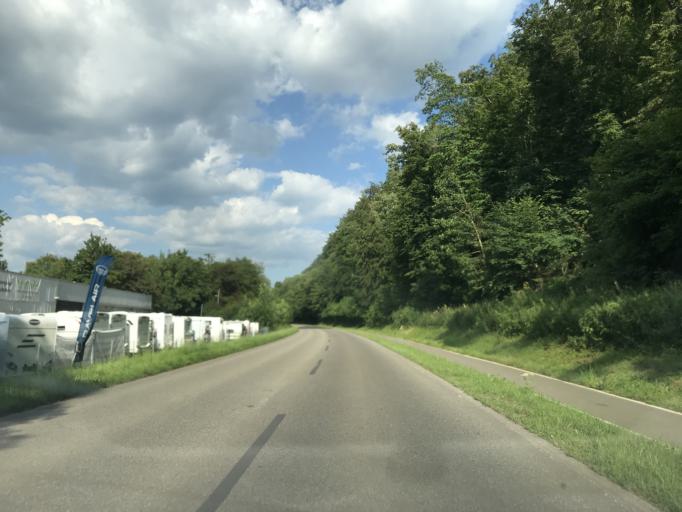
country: DE
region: Baden-Wuerttemberg
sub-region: Freiburg Region
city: Steinen
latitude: 47.6365
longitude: 7.7039
